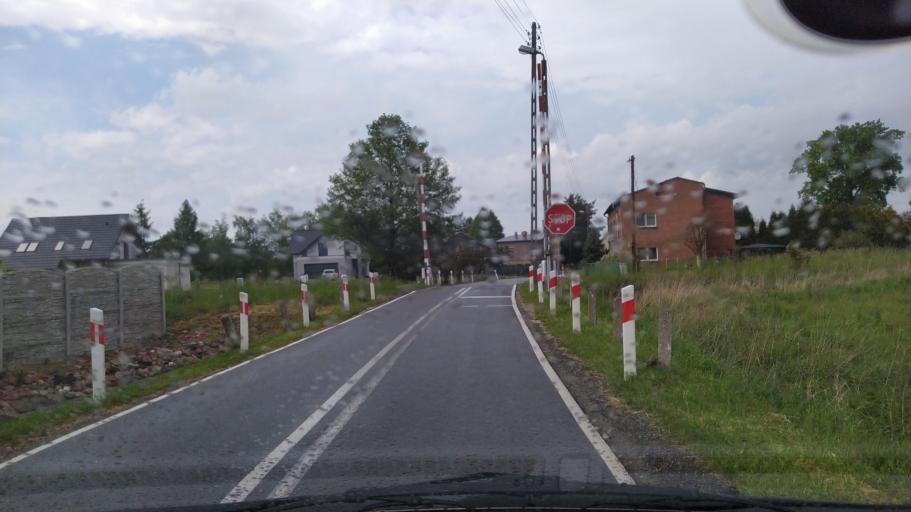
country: PL
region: Silesian Voivodeship
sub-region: Powiat gliwicki
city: Zernica
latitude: 50.2269
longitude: 18.6158
